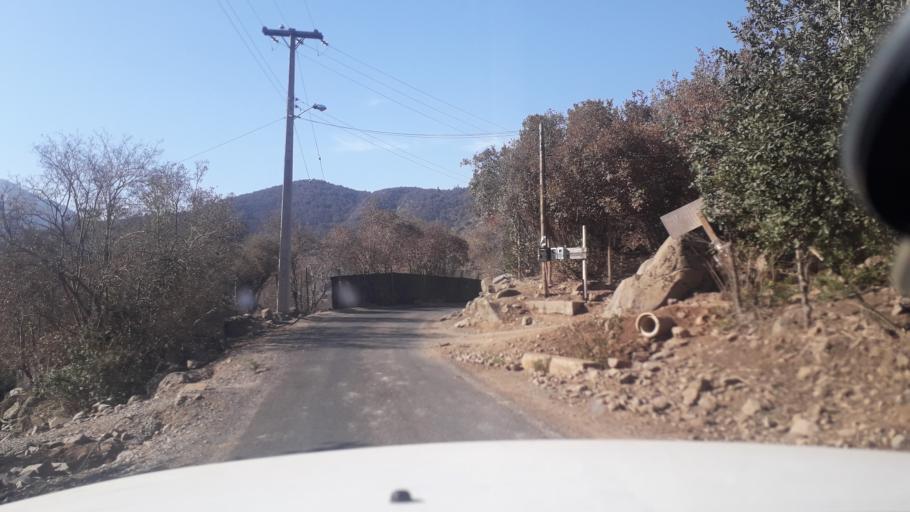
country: CL
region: Valparaiso
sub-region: Provincia de Marga Marga
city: Limache
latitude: -33.0712
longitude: -71.0993
